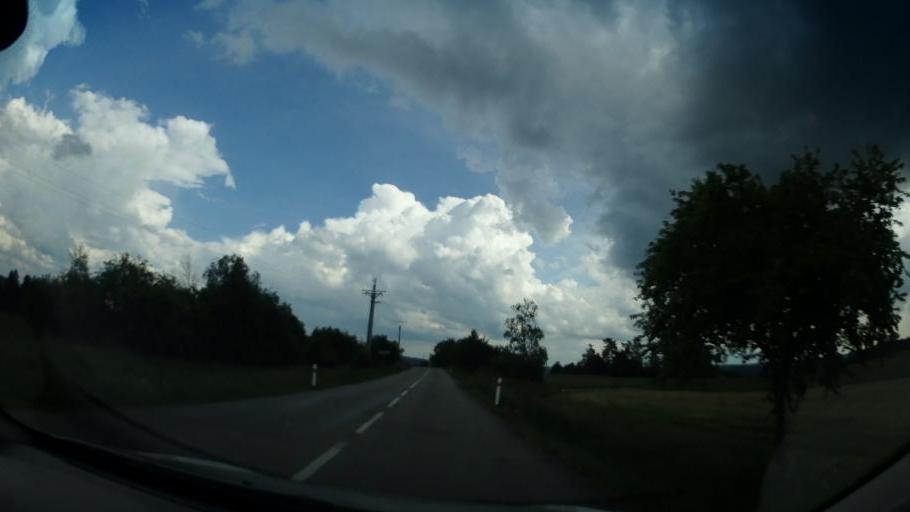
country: CZ
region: South Moravian
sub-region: Okres Brno-Venkov
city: Dolni Loucky
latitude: 49.4021
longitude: 16.3245
